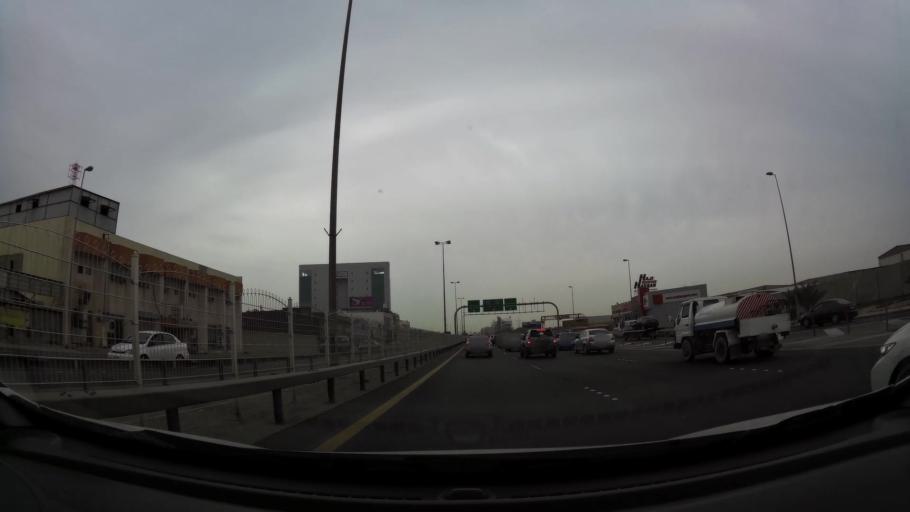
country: BH
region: Northern
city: Madinat `Isa
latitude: 26.1921
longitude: 50.5353
